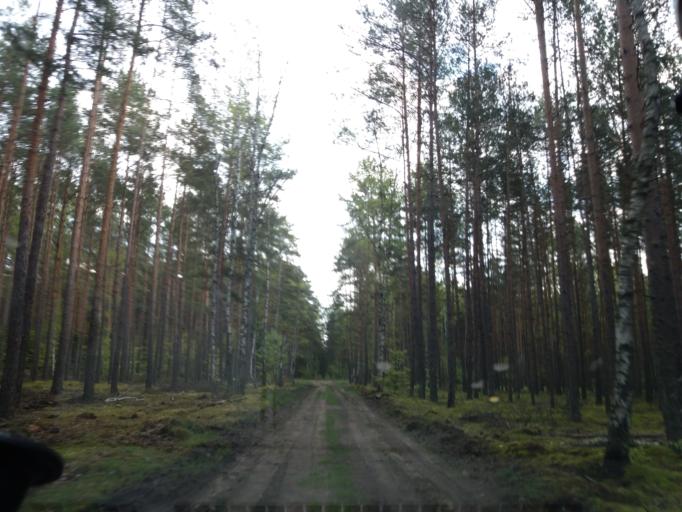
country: PL
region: West Pomeranian Voivodeship
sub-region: Powiat walecki
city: Czlopa
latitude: 53.0957
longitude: 15.9367
